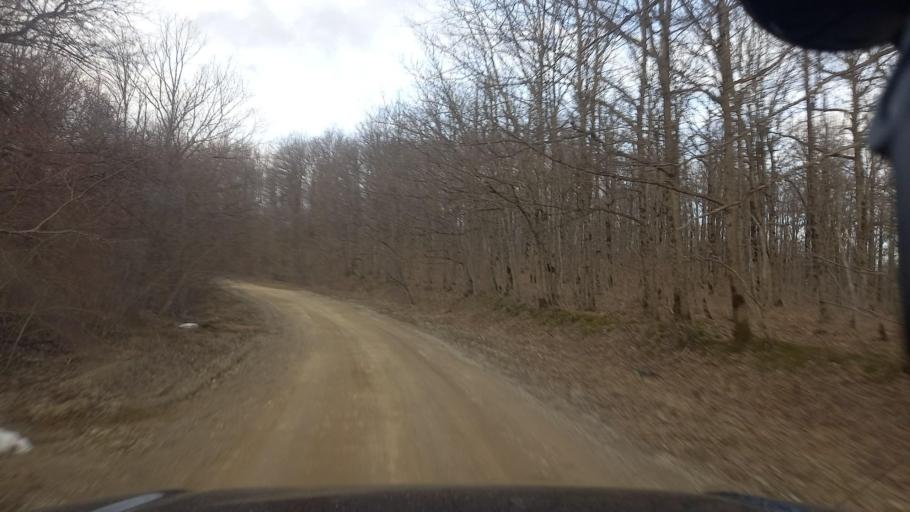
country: RU
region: Krasnodarskiy
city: Goryachiy Klyuch
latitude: 44.6950
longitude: 38.9852
